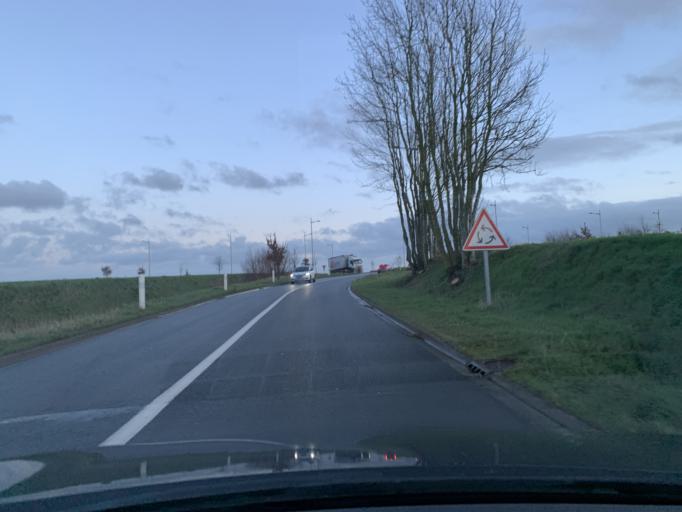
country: FR
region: Nord-Pas-de-Calais
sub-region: Departement du Nord
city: Cambrai
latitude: 50.1530
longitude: 3.2630
